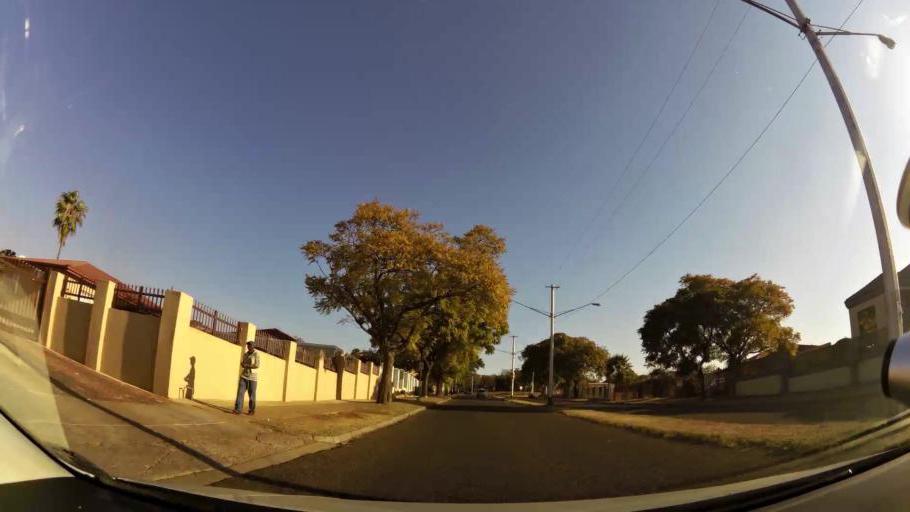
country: ZA
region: Gauteng
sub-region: City of Tshwane Metropolitan Municipality
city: Pretoria
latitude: -25.7551
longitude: 28.1284
